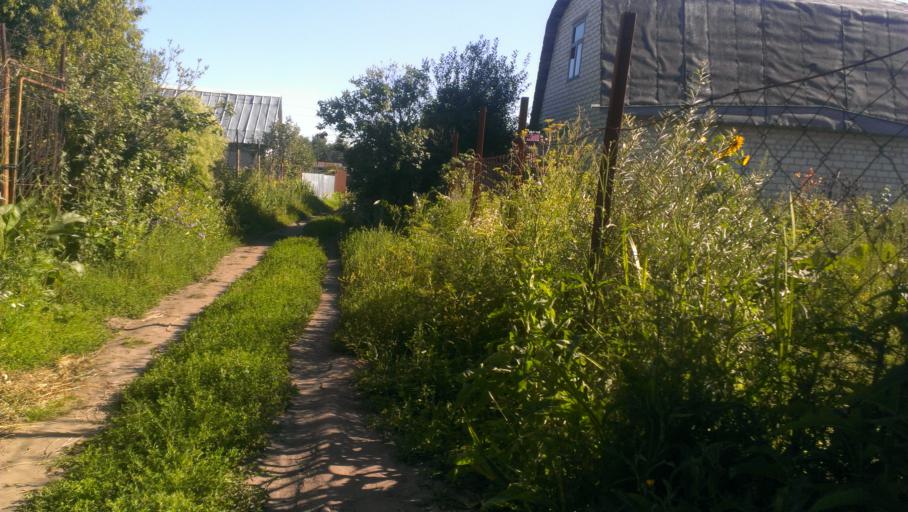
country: RU
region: Altai Krai
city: Novosilikatnyy
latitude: 53.3218
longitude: 83.6696
